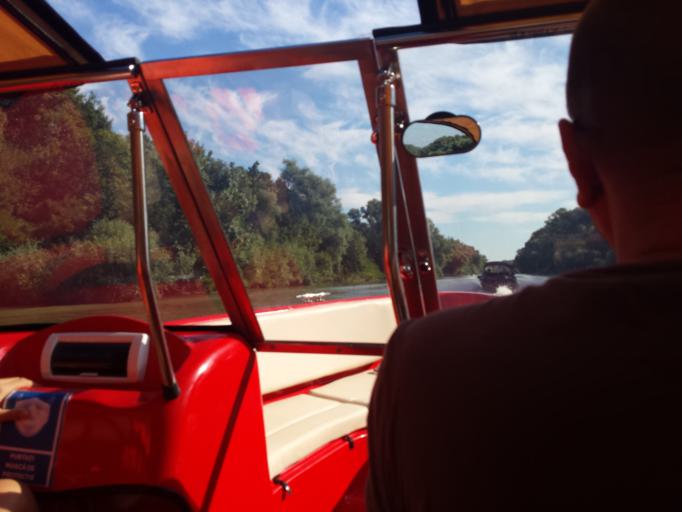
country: RO
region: Tulcea
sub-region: Comuna Nufaru
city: Malcoci
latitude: 45.2153
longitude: 28.8688
